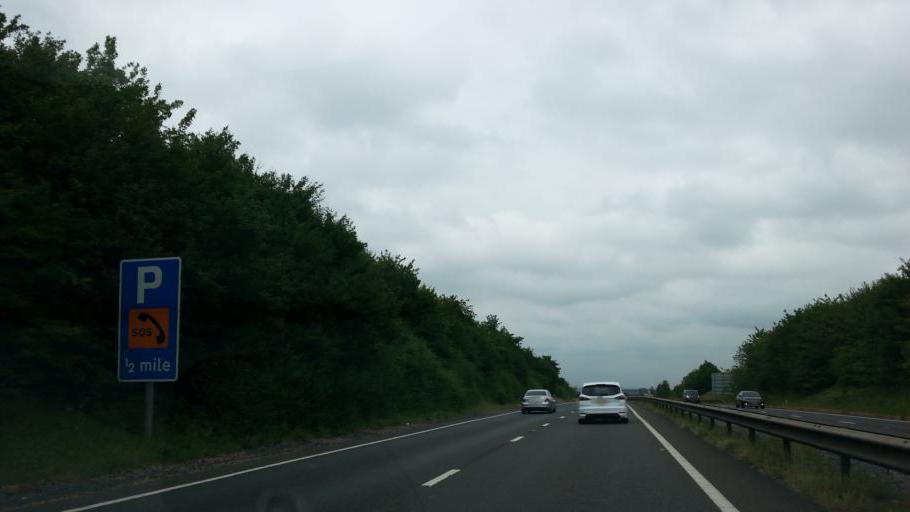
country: GB
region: England
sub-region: Leicestershire
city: Ashby de la Zouch
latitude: 52.7585
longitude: -1.4370
